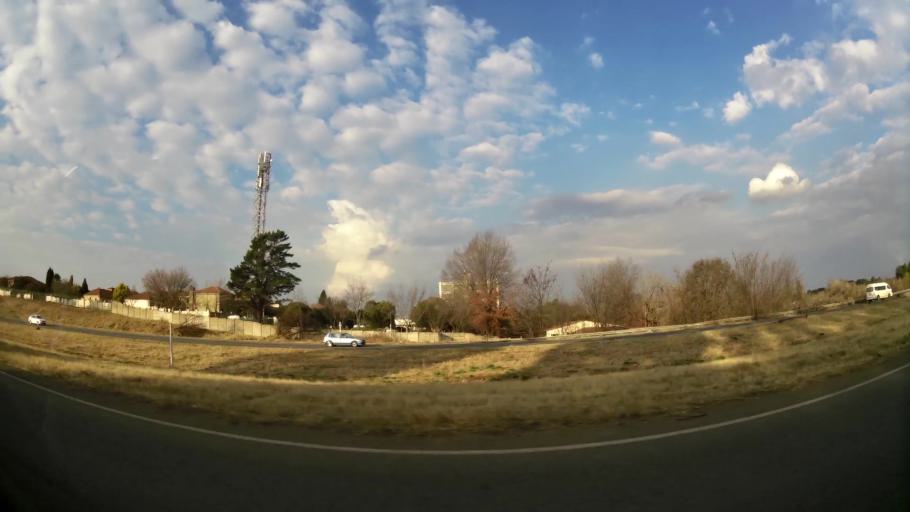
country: ZA
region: Gauteng
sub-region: Sedibeng District Municipality
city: Vanderbijlpark
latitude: -26.7486
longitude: 27.8263
